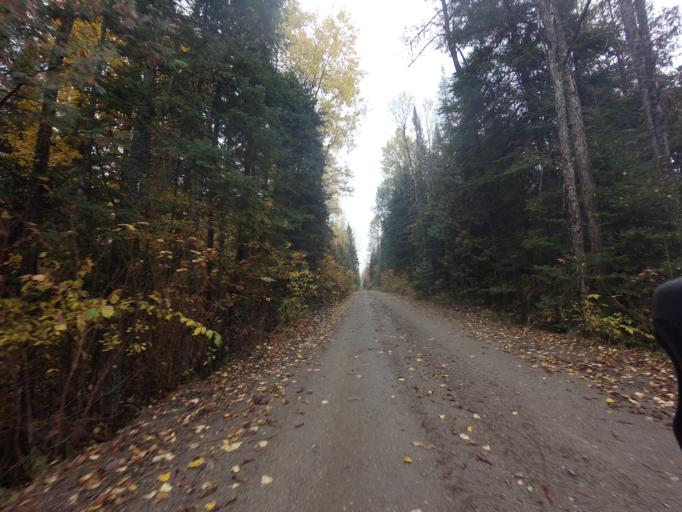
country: CA
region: Ontario
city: Renfrew
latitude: 45.1774
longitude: -76.6828
